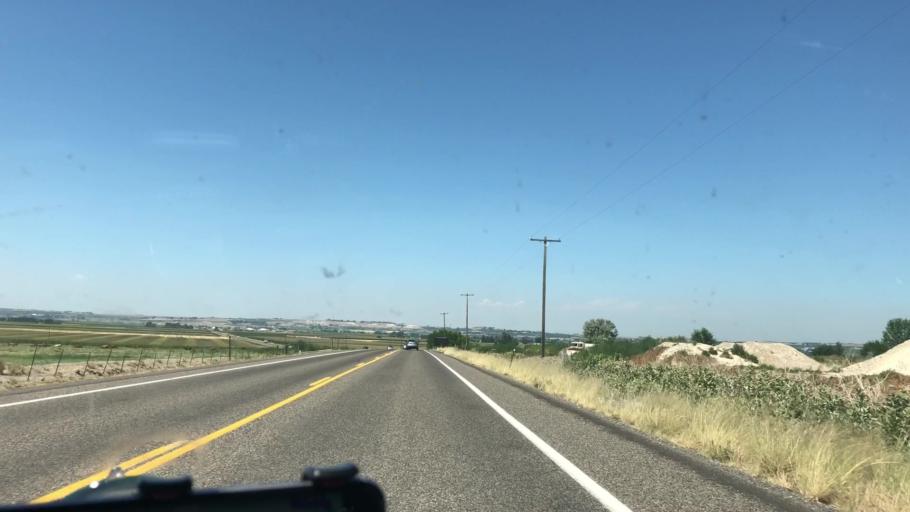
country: US
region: Idaho
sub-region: Owyhee County
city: Marsing
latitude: 43.5197
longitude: -116.8523
